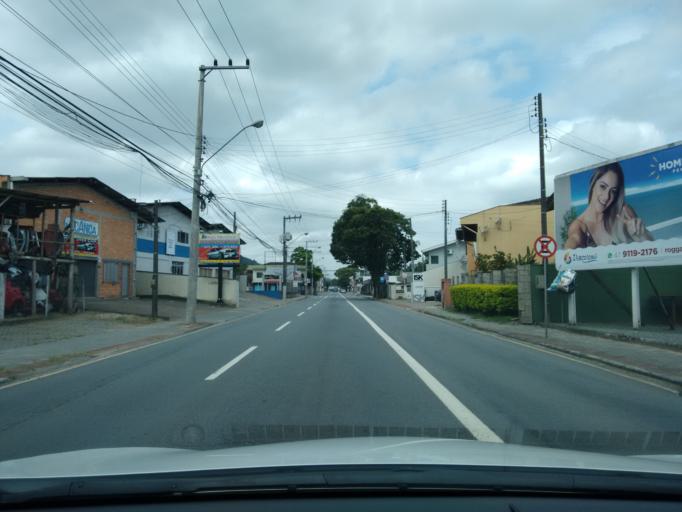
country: BR
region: Santa Catarina
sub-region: Jaragua Do Sul
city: Jaragua do Sul
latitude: -26.4809
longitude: -49.0626
